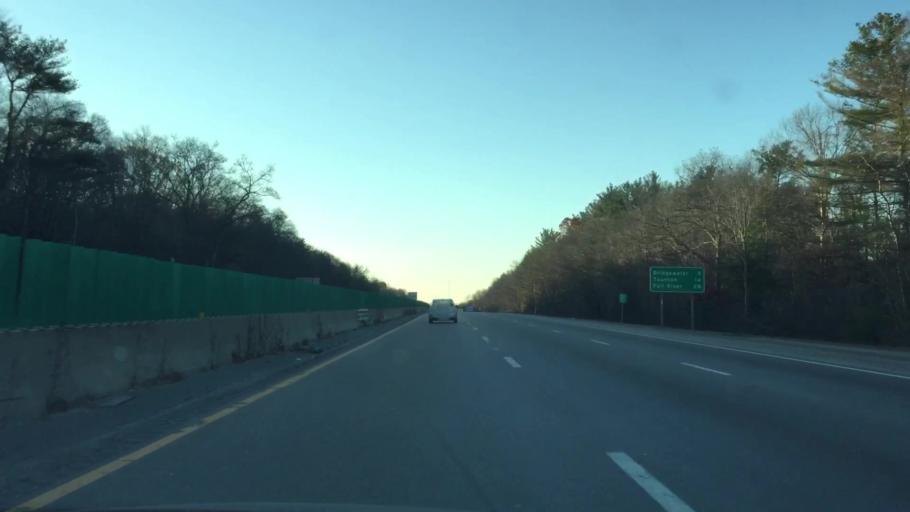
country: US
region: Massachusetts
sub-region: Plymouth County
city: Brockton
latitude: 42.0480
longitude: -71.0572
